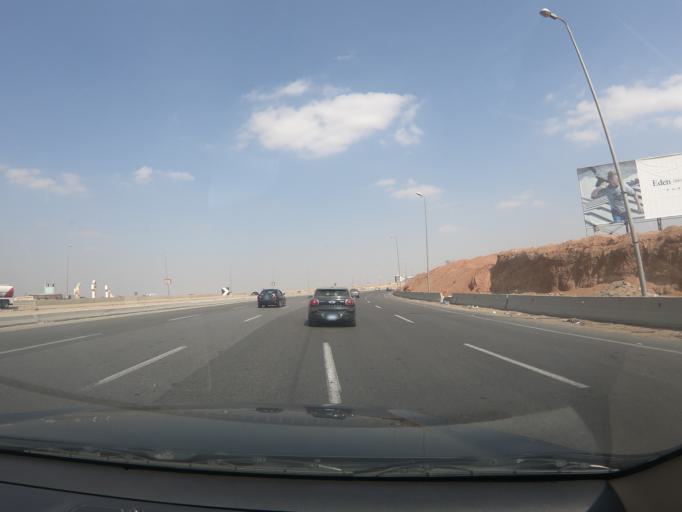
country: EG
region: Muhafazat al Qalyubiyah
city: Al Khankah
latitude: 30.0868
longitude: 31.5204
